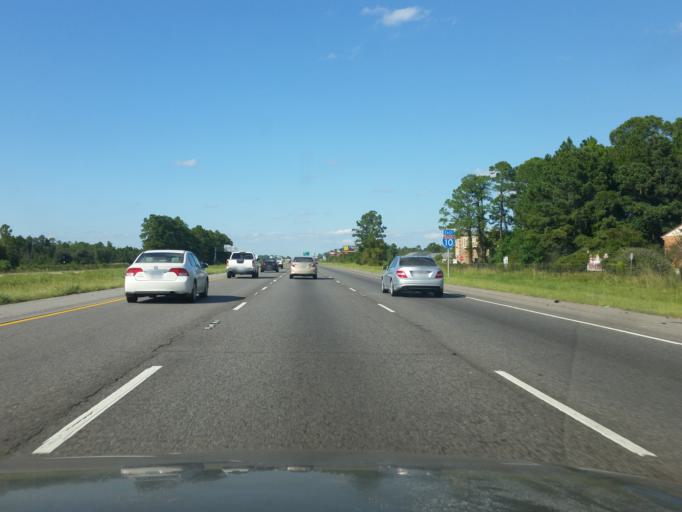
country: US
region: Louisiana
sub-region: Saint Tammany Parish
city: Slidell
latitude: 30.2544
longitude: -89.7608
